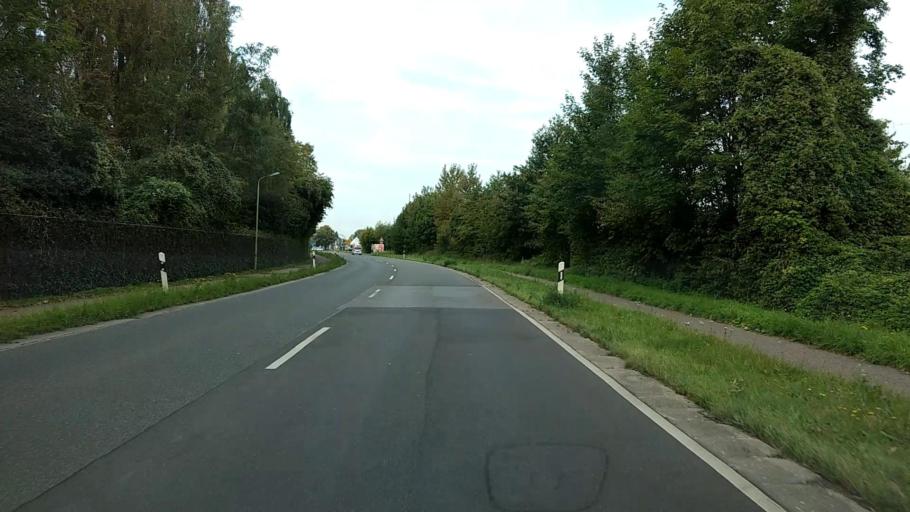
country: DE
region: North Rhine-Westphalia
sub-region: Regierungsbezirk Koln
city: Bergheim
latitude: 50.9475
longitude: 6.6643
